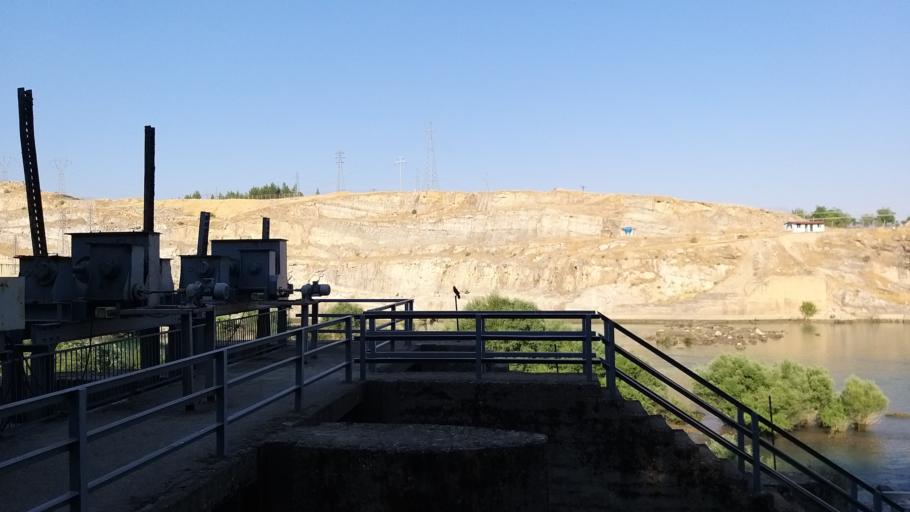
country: TR
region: Diyarbakir
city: Malabadi
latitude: 38.1556
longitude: 41.2017
